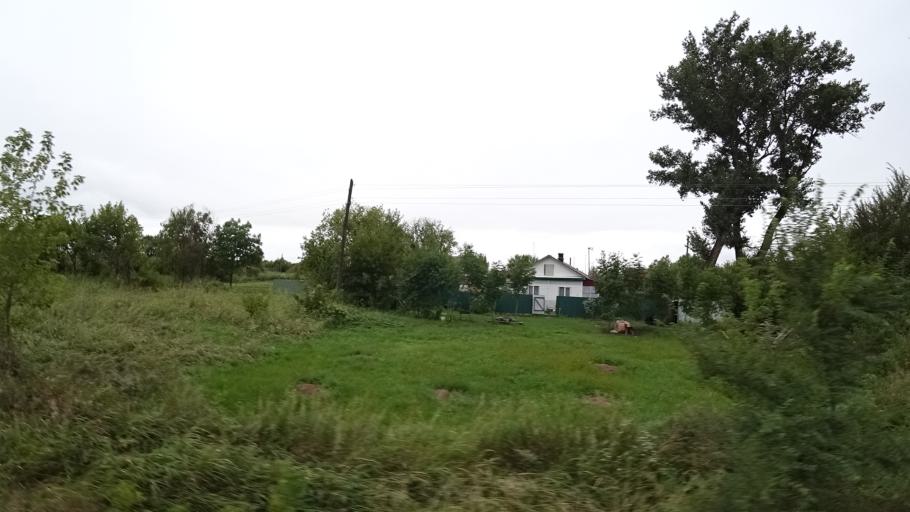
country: RU
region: Primorskiy
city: Chernigovka
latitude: 44.3364
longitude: 132.5262
